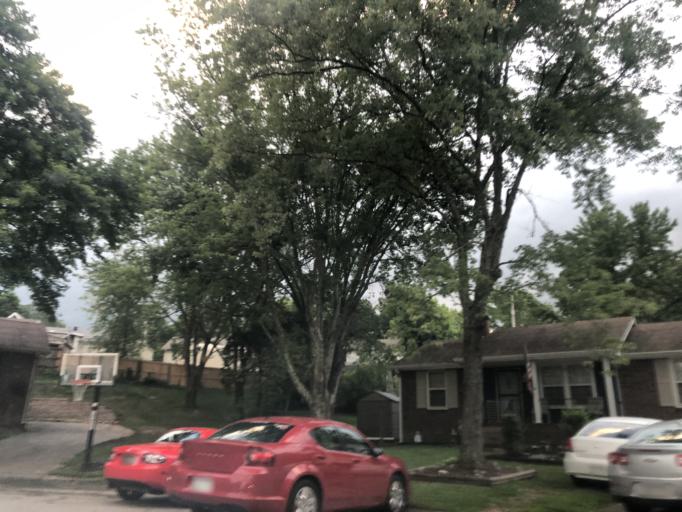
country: US
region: Tennessee
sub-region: Davidson County
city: Lakewood
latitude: 36.1470
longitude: -86.6310
